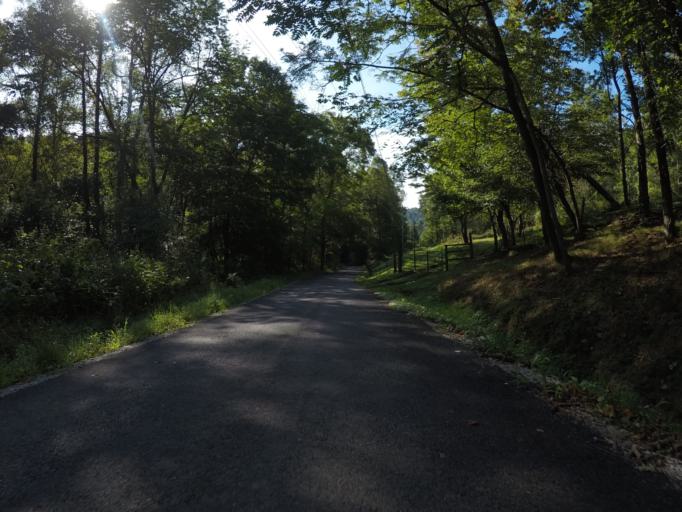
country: US
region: Ohio
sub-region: Lawrence County
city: Burlington
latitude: 38.5205
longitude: -82.5292
